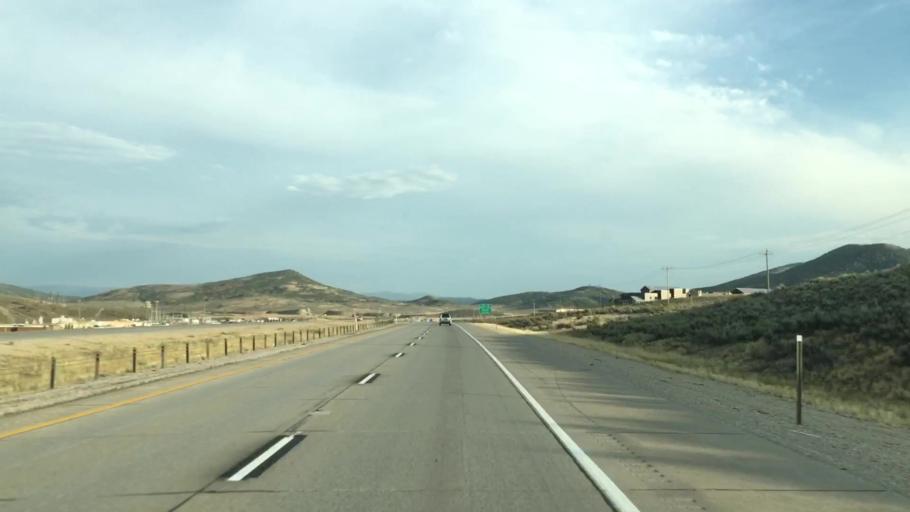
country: US
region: Utah
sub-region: Summit County
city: Park City
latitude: 40.6953
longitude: -111.4711
